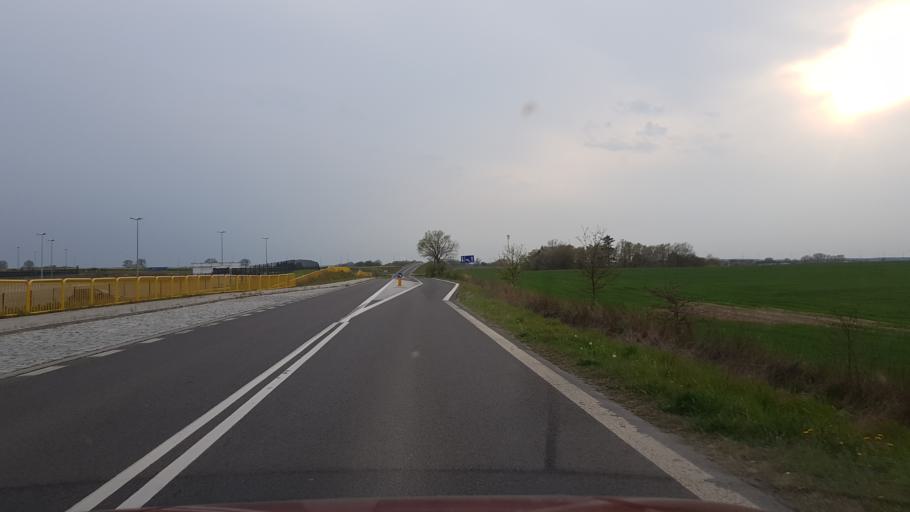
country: PL
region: West Pomeranian Voivodeship
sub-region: Powiat pyrzycki
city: Bielice
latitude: 53.2640
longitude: 14.6384
